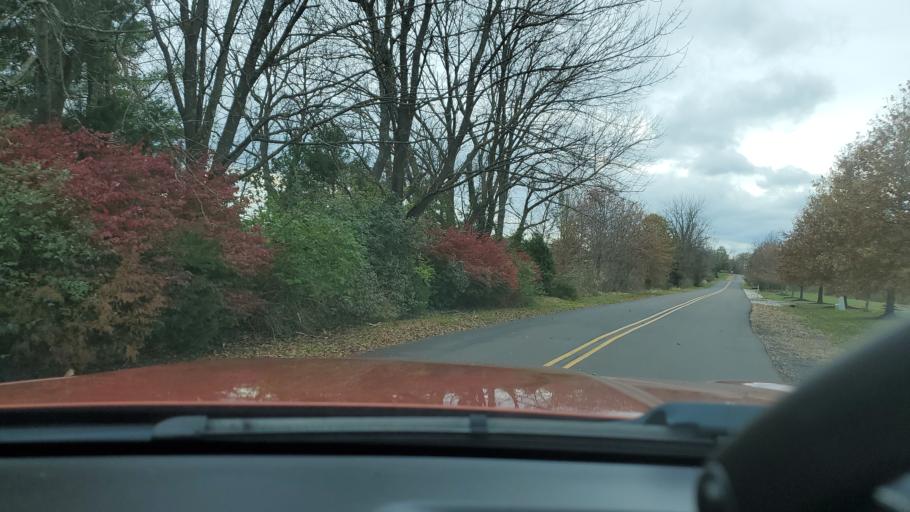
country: US
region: Pennsylvania
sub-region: Montgomery County
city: Spring Mount
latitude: 40.2869
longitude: -75.5070
